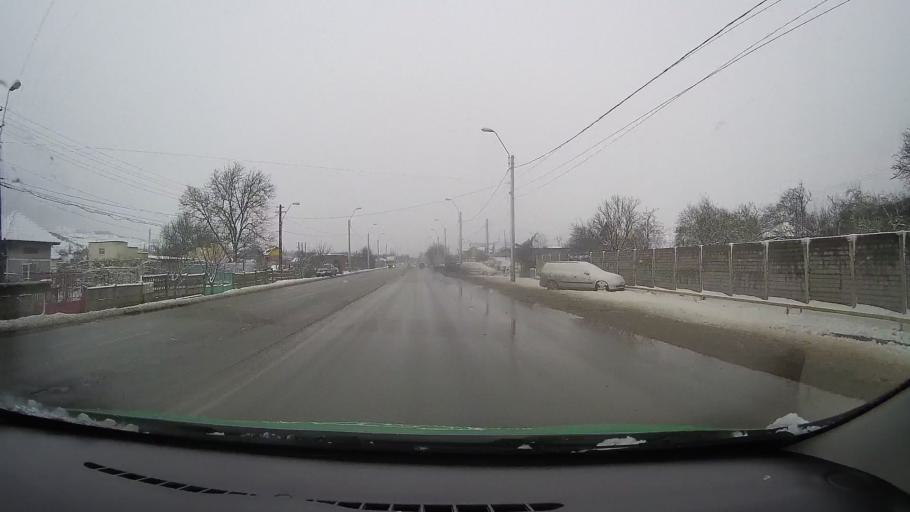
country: RO
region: Hunedoara
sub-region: Municipiul Hunedoara
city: Pestisu Mare
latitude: 45.8018
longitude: 22.9225
